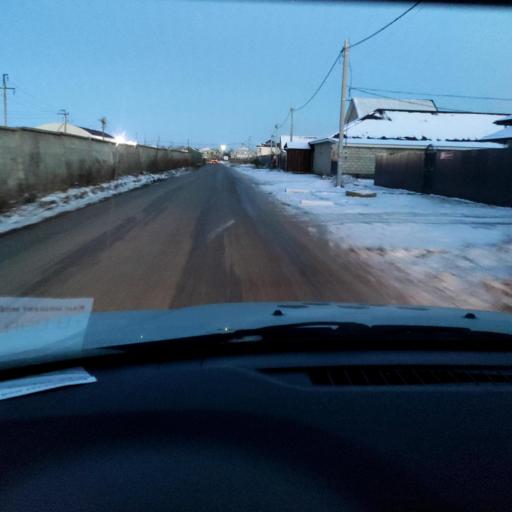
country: RU
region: Samara
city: Tol'yatti
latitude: 53.5721
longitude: 49.4022
